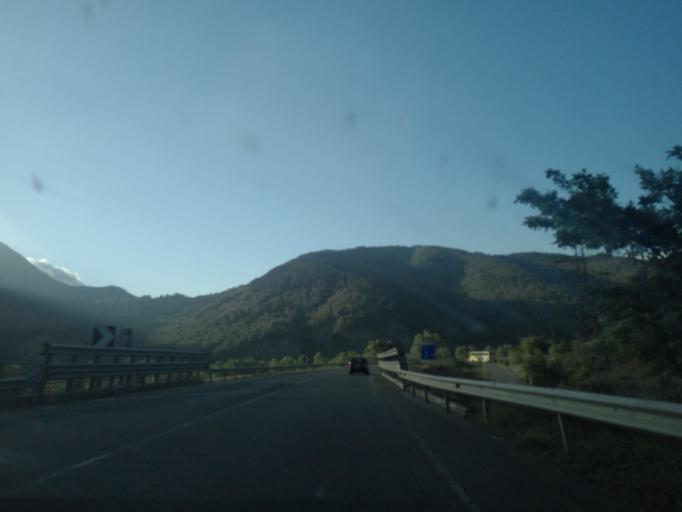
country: AL
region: Lezhe
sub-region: Rrethi i Mirdites
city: Rubik
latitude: 41.7798
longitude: 19.7841
